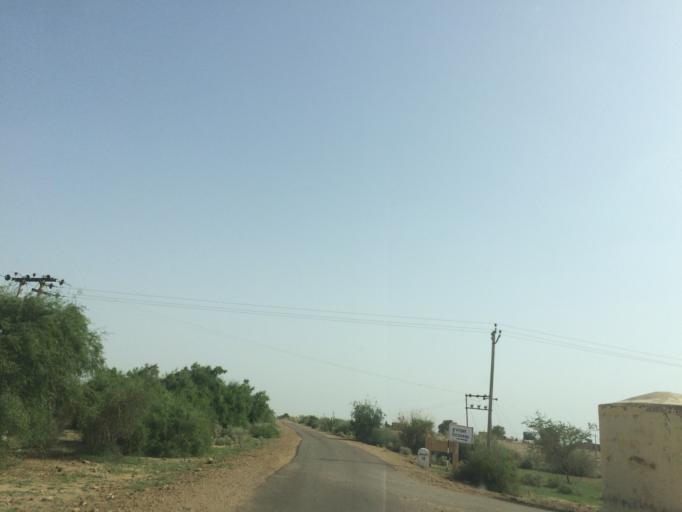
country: IN
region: Rajasthan
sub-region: Jaisalmer
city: Jaisalmer
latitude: 26.8756
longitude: 70.7784
